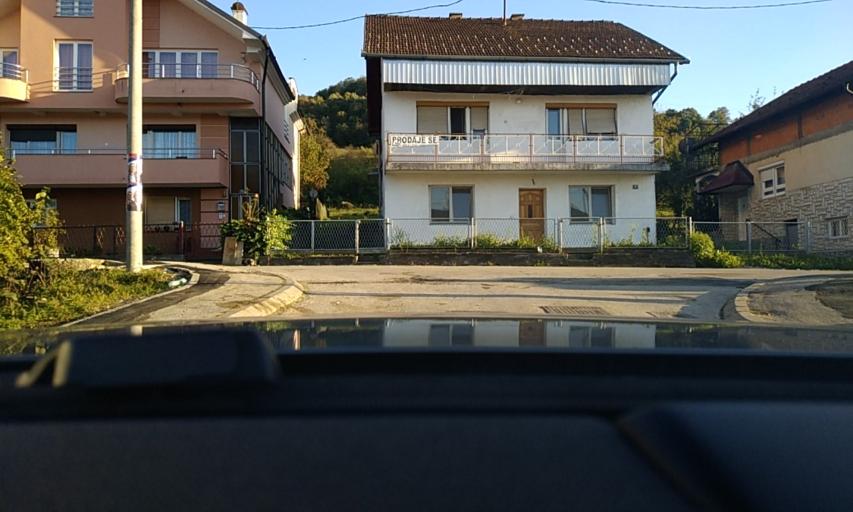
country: BA
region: Republika Srpska
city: Mejdan - Obilicevo
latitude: 44.7564
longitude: 17.1933
